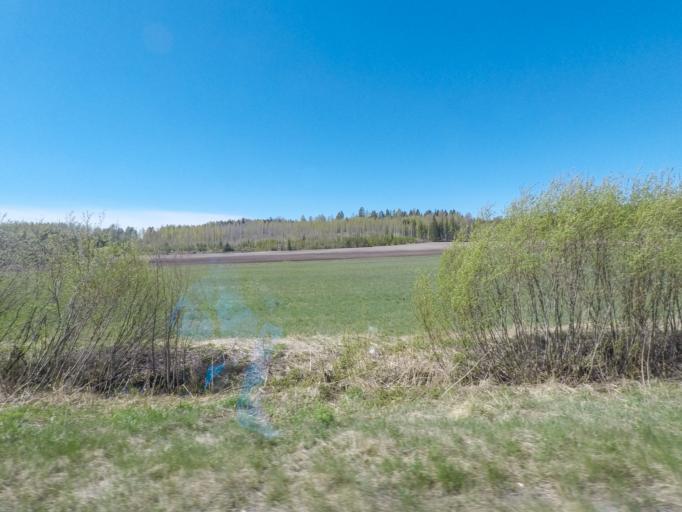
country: FI
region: Uusimaa
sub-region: Helsinki
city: Sammatti
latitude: 60.3920
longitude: 23.8128
